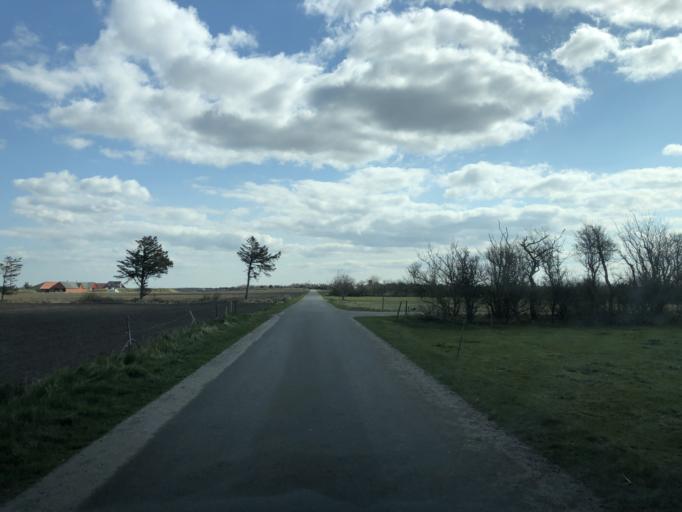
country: DK
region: Central Jutland
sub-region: Holstebro Kommune
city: Ulfborg
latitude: 56.4009
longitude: 8.2081
